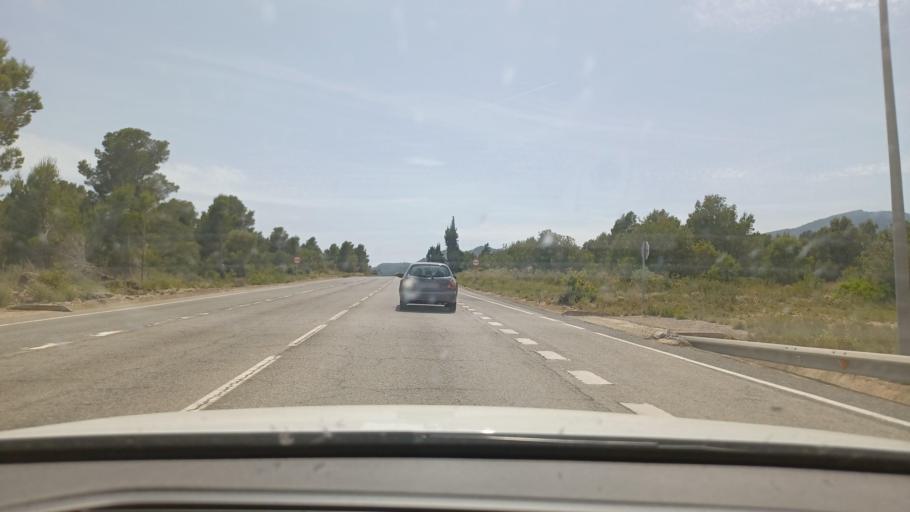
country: ES
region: Catalonia
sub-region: Provincia de Tarragona
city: Colldejou
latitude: 40.9877
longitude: 0.9077
